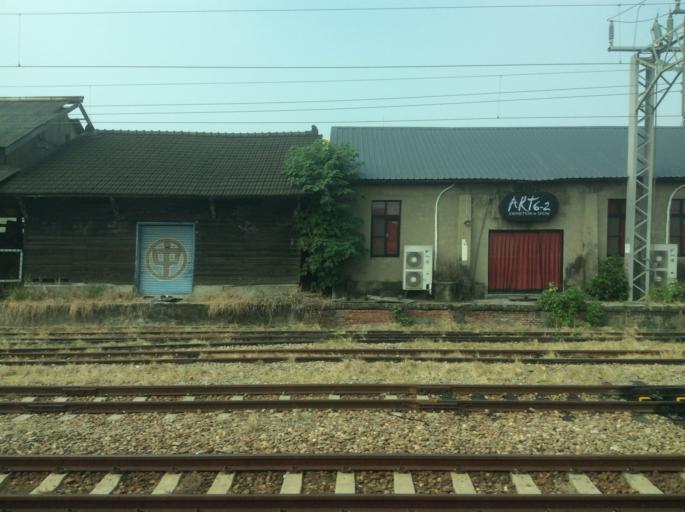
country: TW
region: Taiwan
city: Xinying
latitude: 23.3078
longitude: 120.3239
